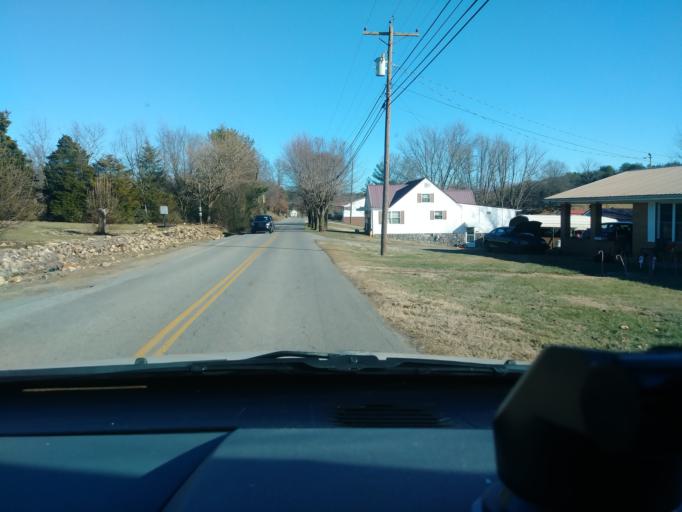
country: US
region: Tennessee
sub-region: Greene County
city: Greeneville
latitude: 36.1126
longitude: -82.8756
